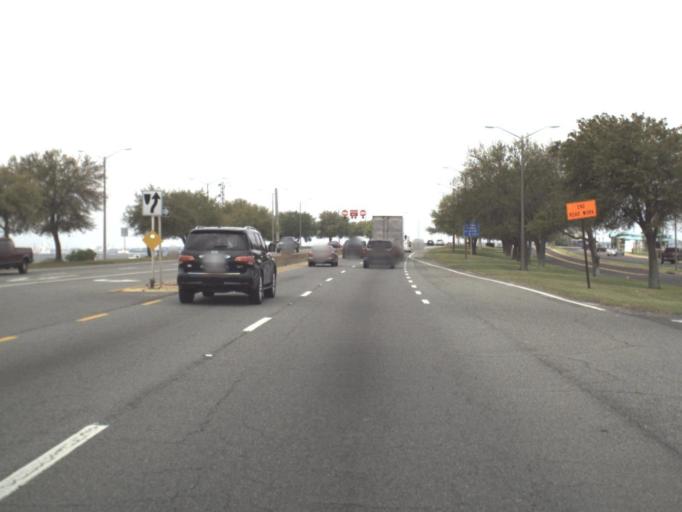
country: US
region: Florida
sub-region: Santa Rosa County
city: Gulf Breeze
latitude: 30.3715
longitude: -87.1762
